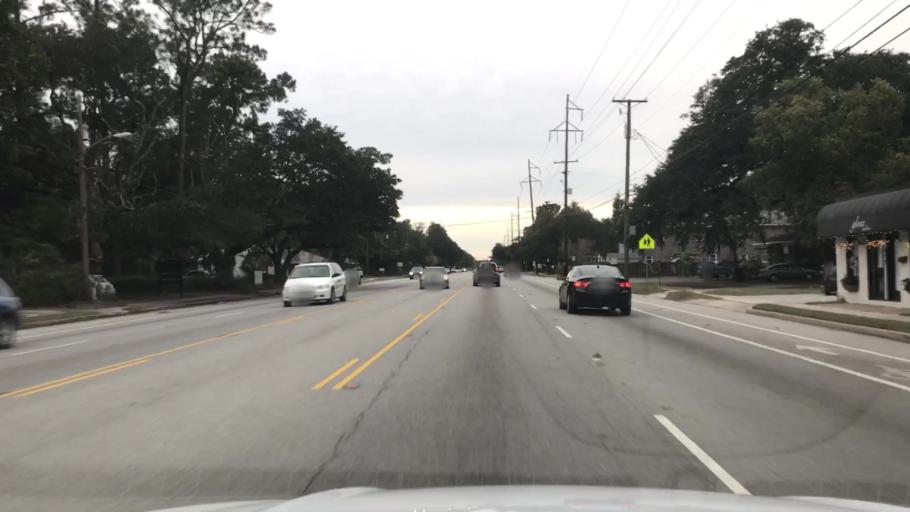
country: US
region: South Carolina
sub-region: Charleston County
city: Charleston
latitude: 32.7863
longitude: -79.9804
